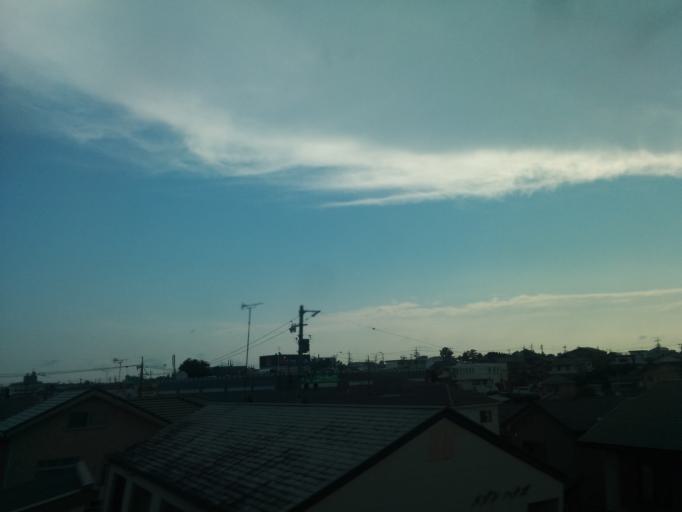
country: JP
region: Aichi
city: Toyohashi
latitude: 34.7459
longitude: 137.3933
